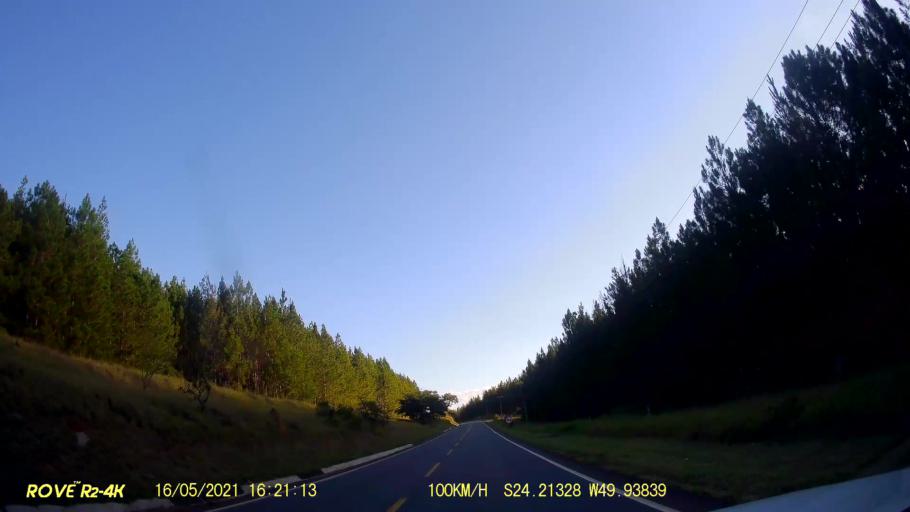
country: BR
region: Parana
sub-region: Jaguariaiva
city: Jaguariaiva
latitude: -24.2134
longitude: -49.9385
